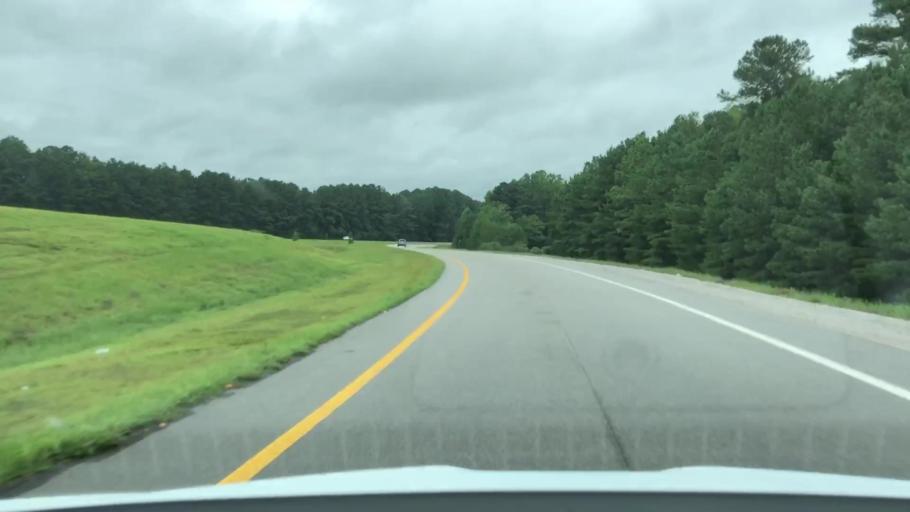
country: US
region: North Carolina
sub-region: Wilson County
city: Lucama
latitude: 35.7336
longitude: -78.0091
